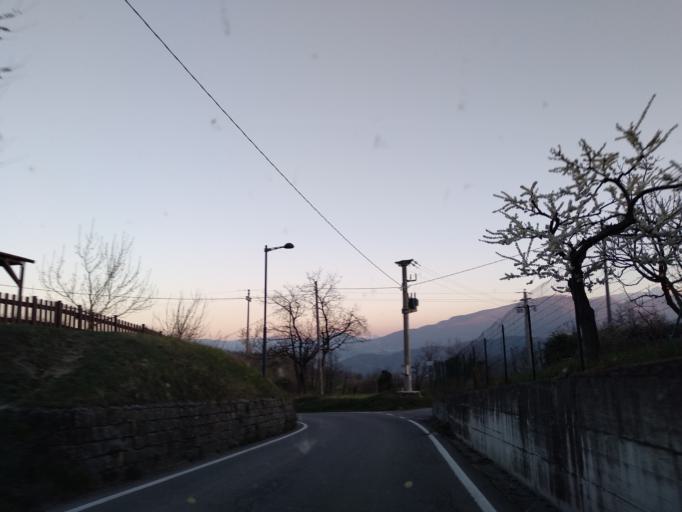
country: IT
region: Emilia-Romagna
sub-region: Provincia di Reggio Emilia
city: Castelnovo ne'Monti
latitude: 44.4145
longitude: 10.4009
